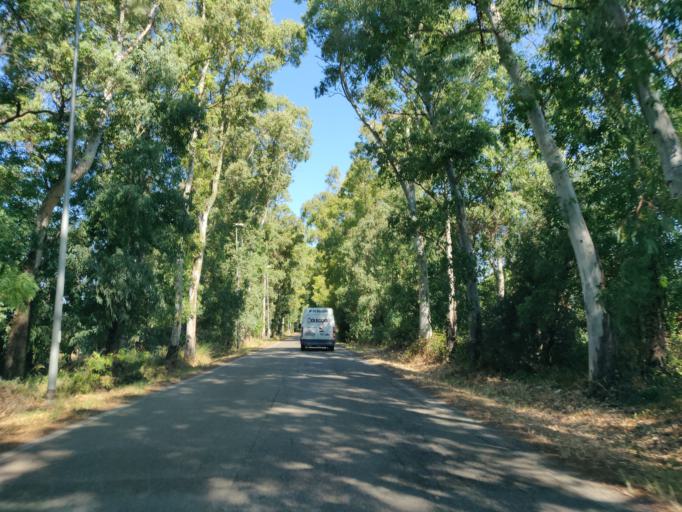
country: IT
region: Latium
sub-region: Citta metropolitana di Roma Capitale
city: Aurelia
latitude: 42.1571
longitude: 11.7525
